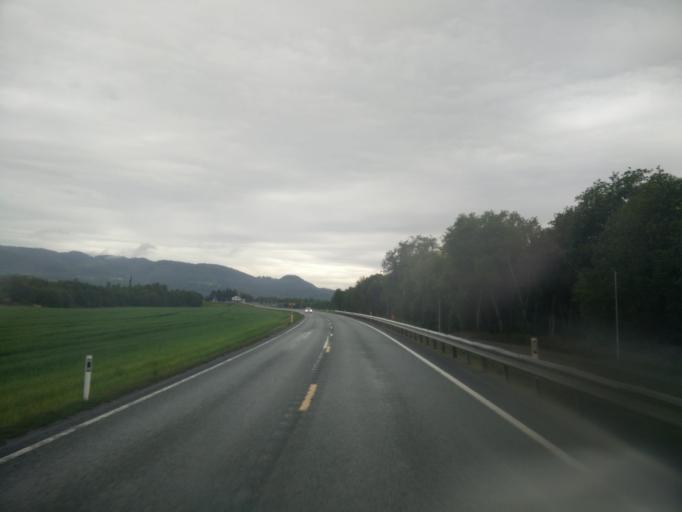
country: NO
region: Sor-Trondelag
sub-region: Orkdal
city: Orkanger
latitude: 63.2718
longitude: 9.8051
